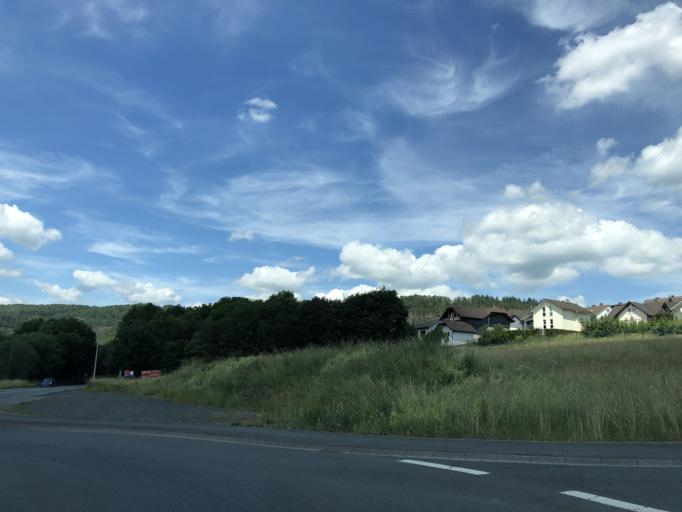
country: DE
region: North Rhine-Westphalia
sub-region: Regierungsbezirk Arnsberg
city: Bad Laasphe
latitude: 50.9298
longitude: 8.4342
